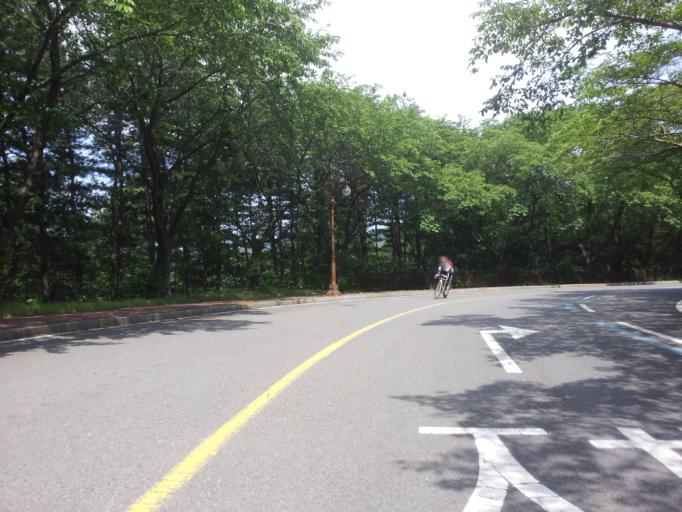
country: KR
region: Daejeon
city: Sintansin
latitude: 36.4744
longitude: 127.4791
